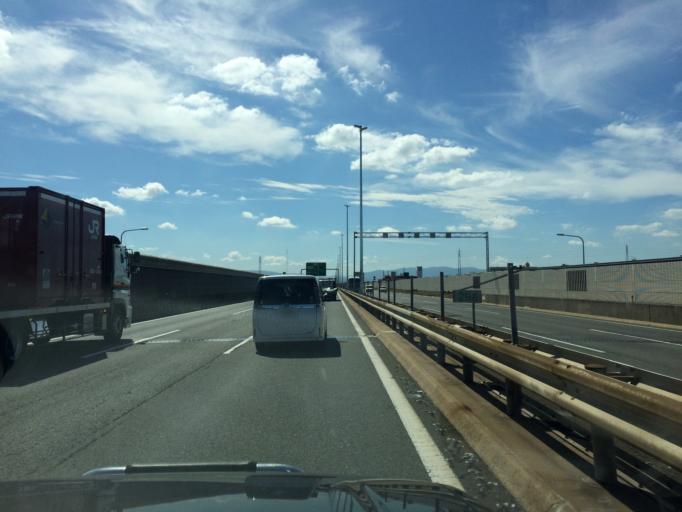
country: JP
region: Osaka
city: Matsubara
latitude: 34.5754
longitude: 135.5633
